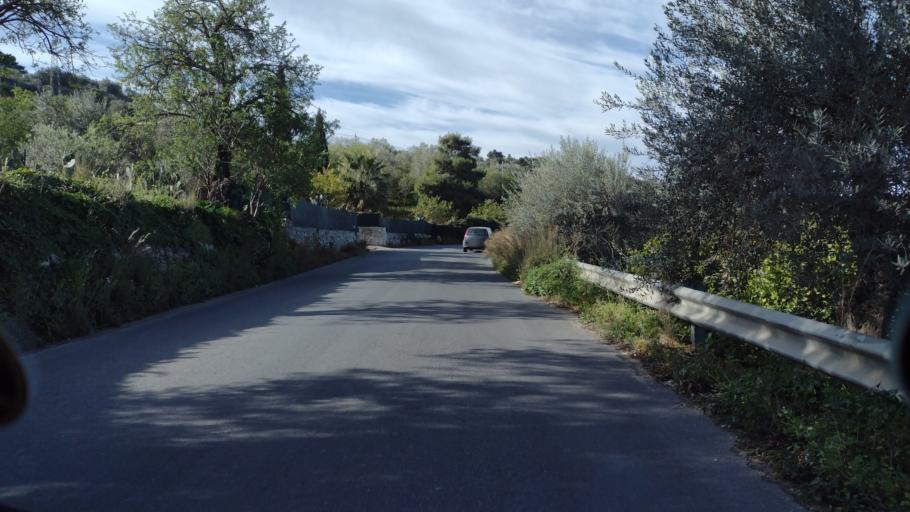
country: IT
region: Sicily
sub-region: Provincia di Siracusa
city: Noto
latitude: 36.8778
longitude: 15.0877
